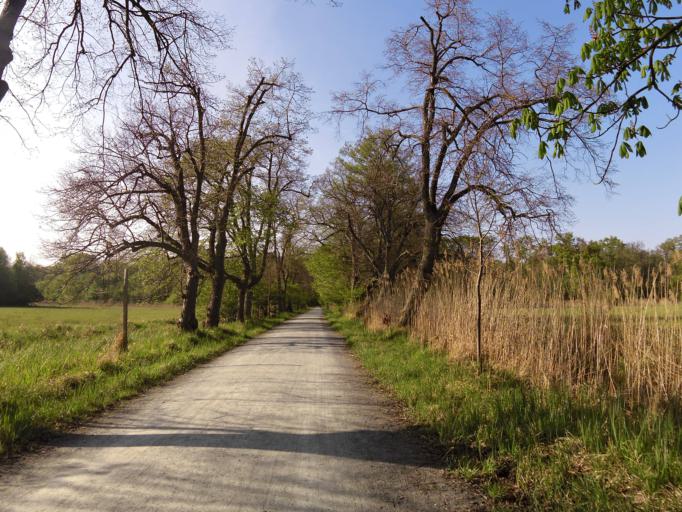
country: DE
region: Hesse
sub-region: Regierungsbezirk Darmstadt
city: Nauheim
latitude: 49.9822
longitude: 8.5049
